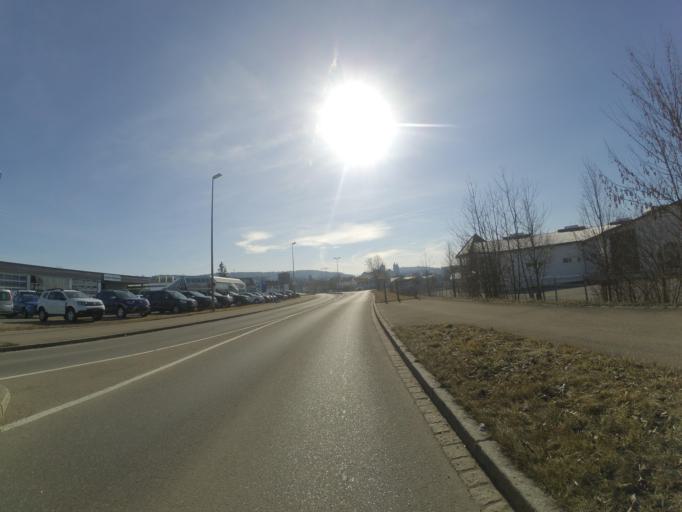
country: DE
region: Baden-Wuerttemberg
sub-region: Tuebingen Region
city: Weingarten
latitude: 47.8183
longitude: 9.6407
